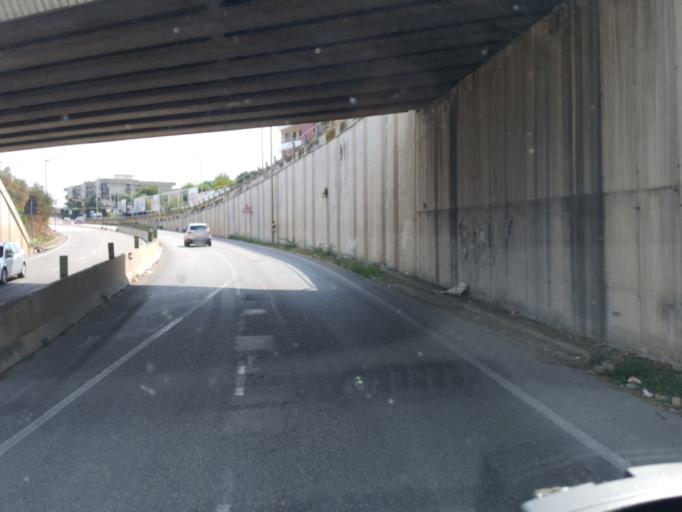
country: IT
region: Apulia
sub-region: Provincia di Bari
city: Modugno
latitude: 41.0922
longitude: 16.7764
